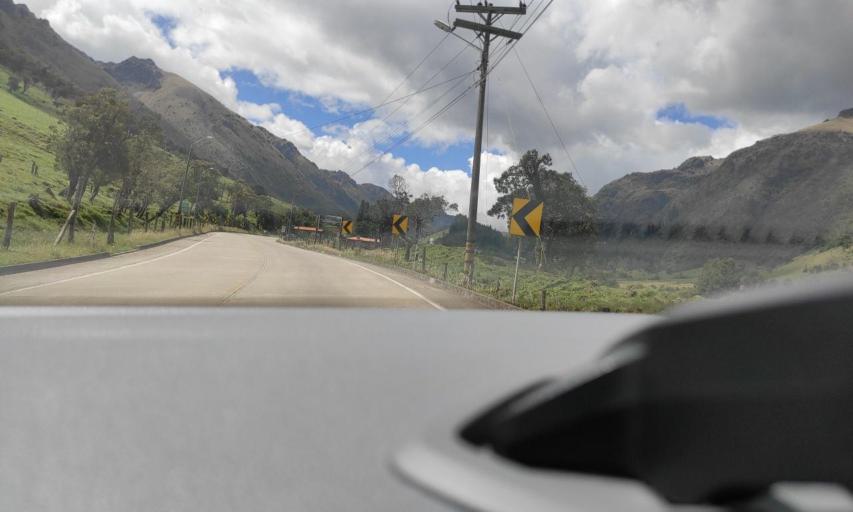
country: EC
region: Azuay
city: Cuenca
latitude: -2.8282
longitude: -79.1368
